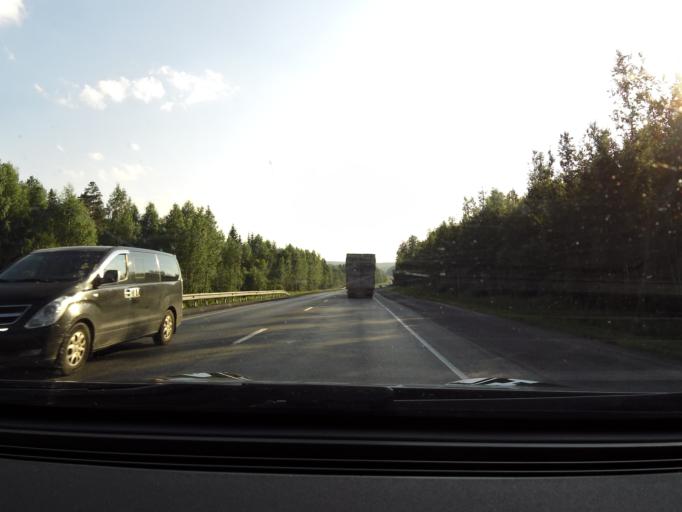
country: RU
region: Sverdlovsk
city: Druzhinino
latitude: 56.8402
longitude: 59.6628
